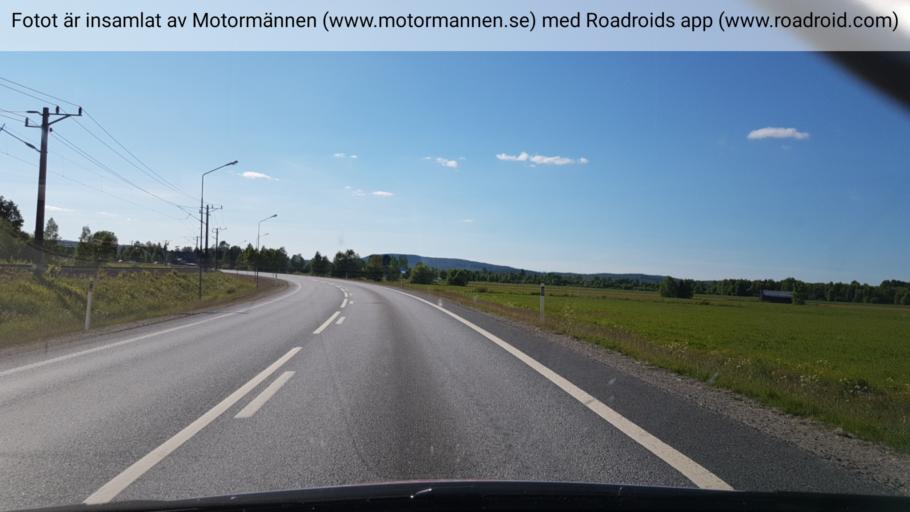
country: SE
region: Vaesterbotten
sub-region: Vannas Kommun
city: Vannasby
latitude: 63.9207
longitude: 19.8689
